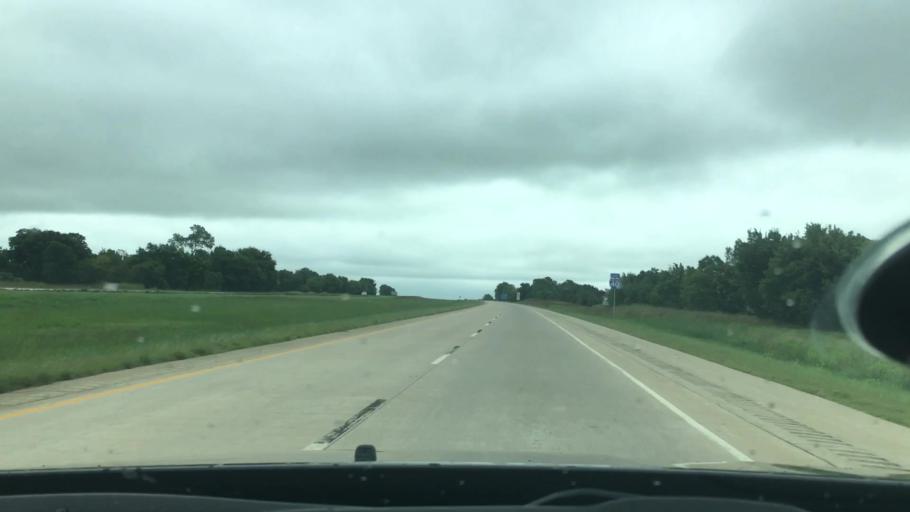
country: US
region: Oklahoma
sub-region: McIntosh County
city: Checotah
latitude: 35.4569
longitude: -95.5851
